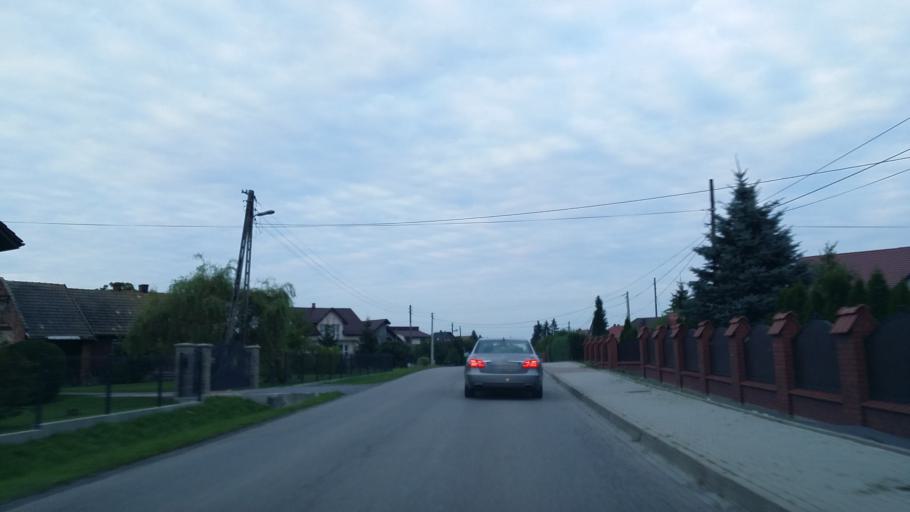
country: PL
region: Lesser Poland Voivodeship
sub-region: Powiat krakowski
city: Kaszow
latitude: 50.0176
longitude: 19.7213
